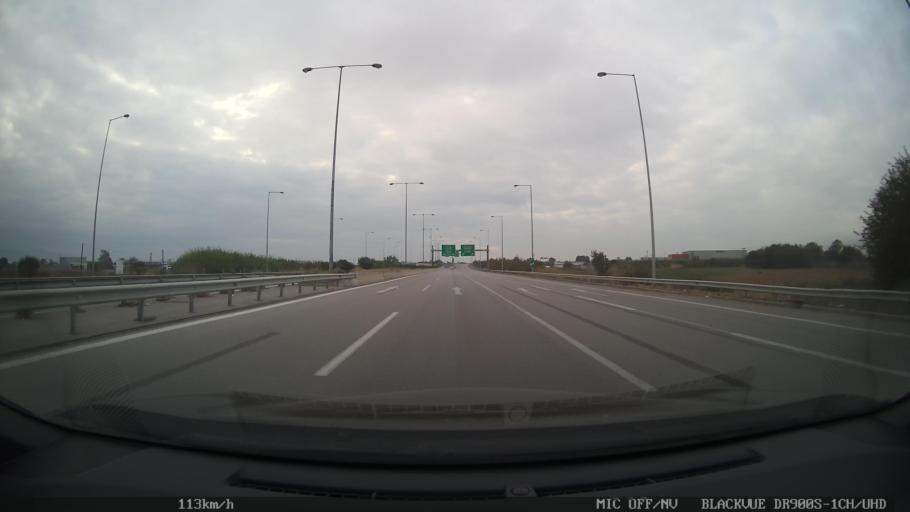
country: GR
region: Central Macedonia
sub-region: Nomos Thessalonikis
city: Kalochori
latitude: 40.6593
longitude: 22.8396
